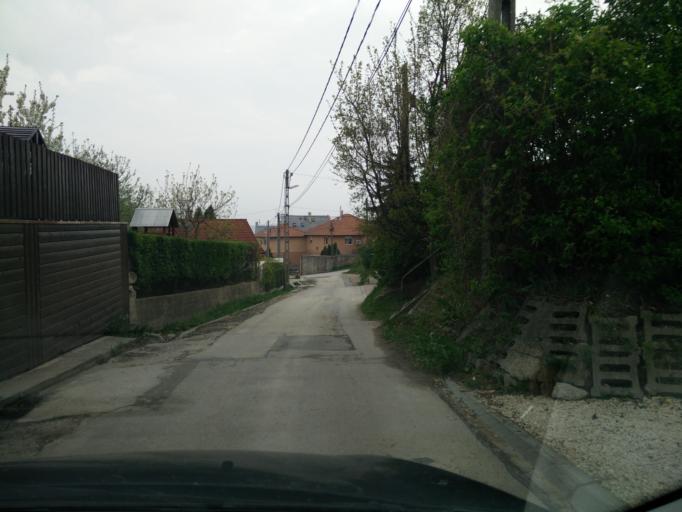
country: HU
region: Pest
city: Budaors
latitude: 47.4678
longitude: 18.9584
